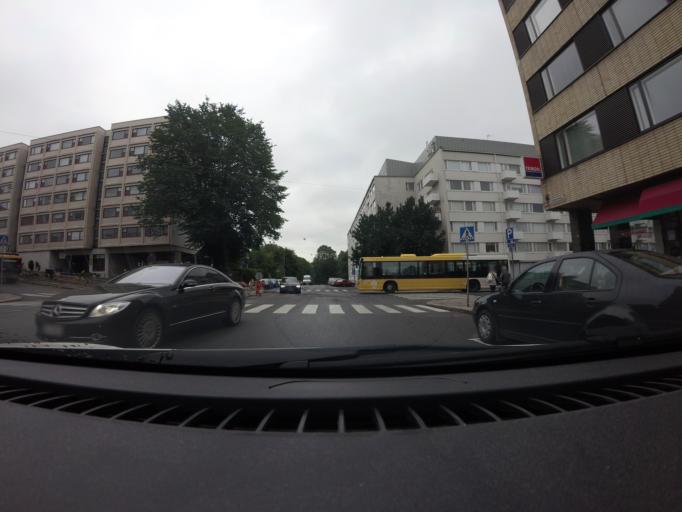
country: FI
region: Varsinais-Suomi
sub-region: Turku
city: Turku
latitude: 60.4546
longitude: 22.2737
